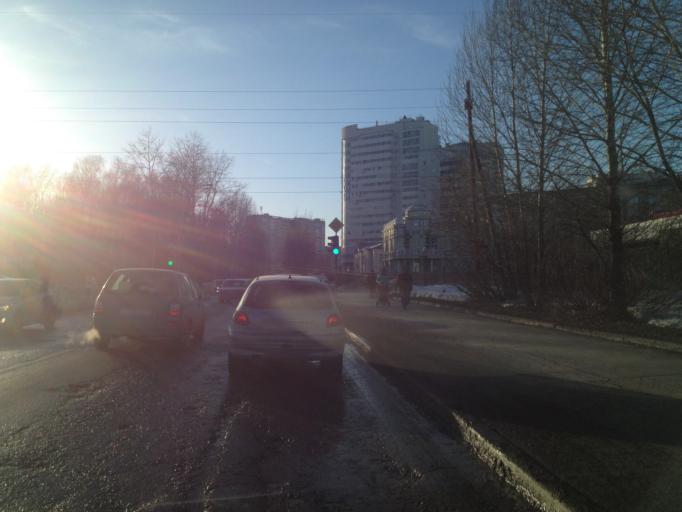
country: RU
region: Sverdlovsk
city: Yekaterinburg
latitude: 56.8656
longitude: 60.5671
